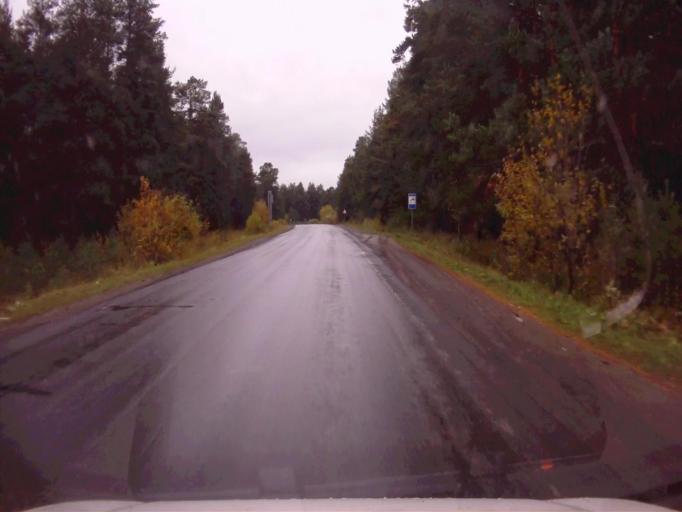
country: RU
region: Chelyabinsk
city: Verkhniy Ufaley
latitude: 56.0534
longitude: 60.1698
